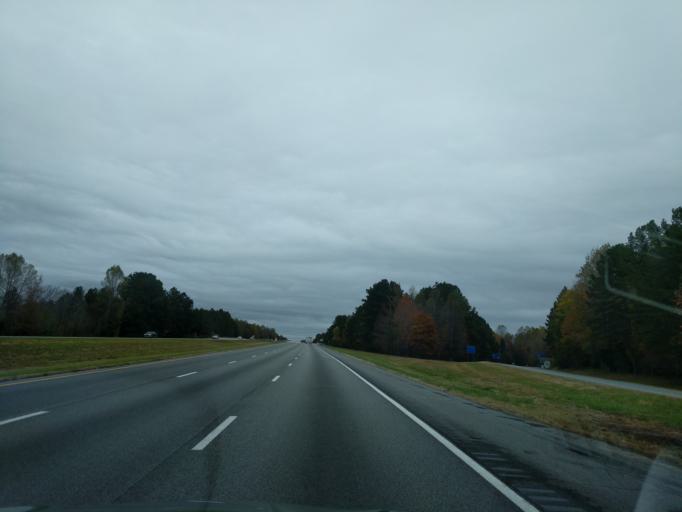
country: US
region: North Carolina
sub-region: Davidson County
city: Lexington
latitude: 35.8074
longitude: -80.1840
